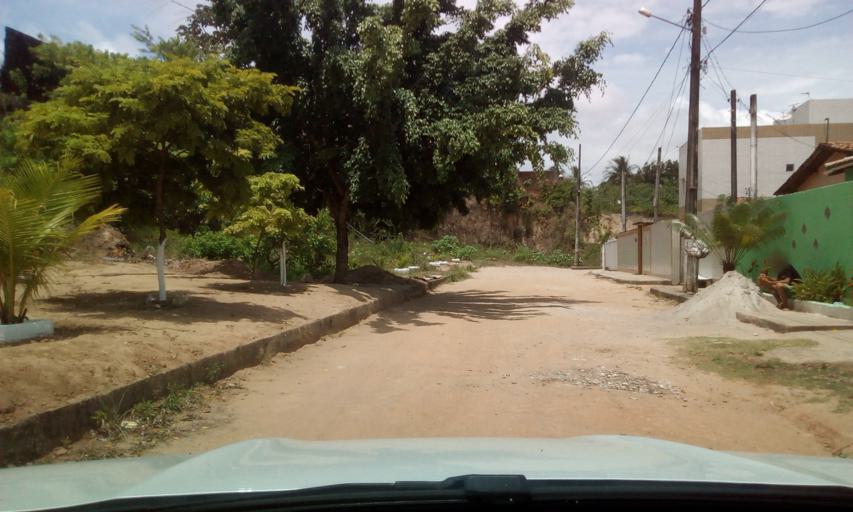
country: BR
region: Paraiba
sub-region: Joao Pessoa
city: Joao Pessoa
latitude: -7.1706
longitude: -34.8832
